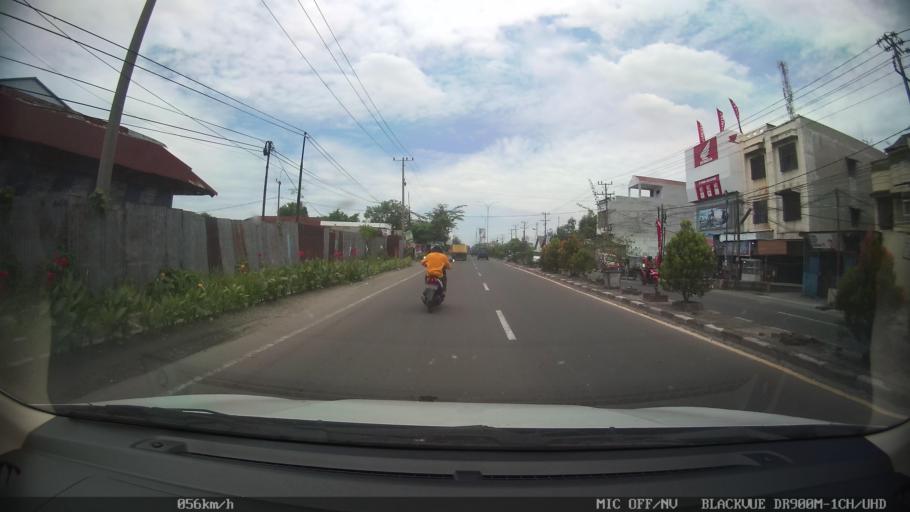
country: ID
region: North Sumatra
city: Sunggal
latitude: 3.5995
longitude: 98.5842
